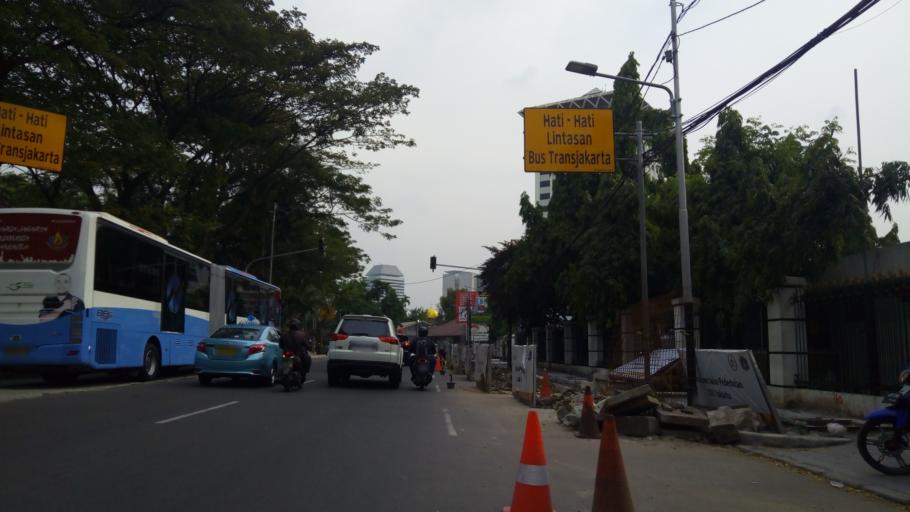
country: ID
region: Jakarta Raya
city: Jakarta
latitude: -6.1738
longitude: 106.8334
